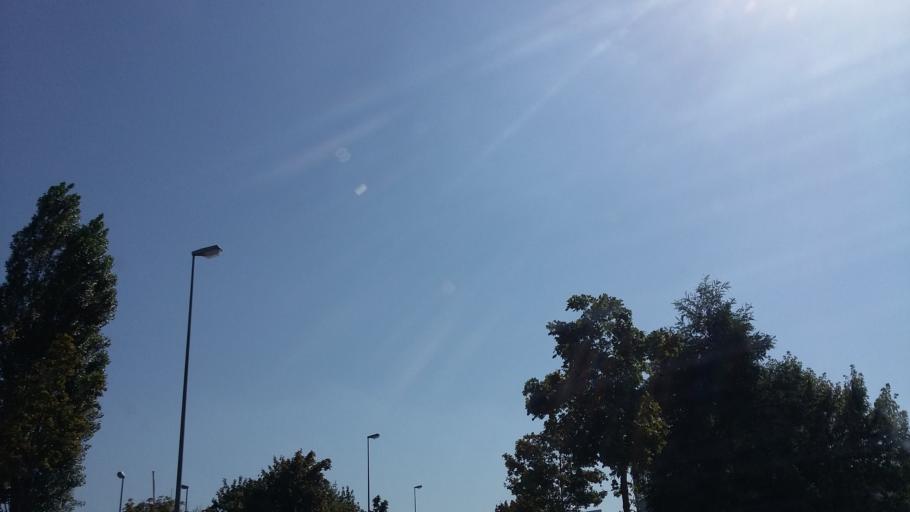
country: DE
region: Bavaria
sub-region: Swabia
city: Augsburg
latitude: 48.3462
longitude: 10.8859
